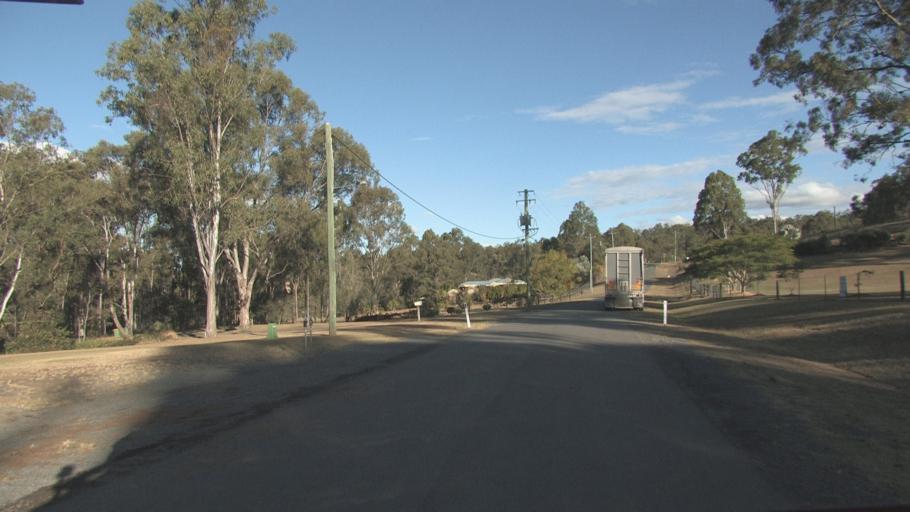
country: AU
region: Queensland
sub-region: Logan
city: Cedar Vale
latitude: -27.9292
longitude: 153.0521
